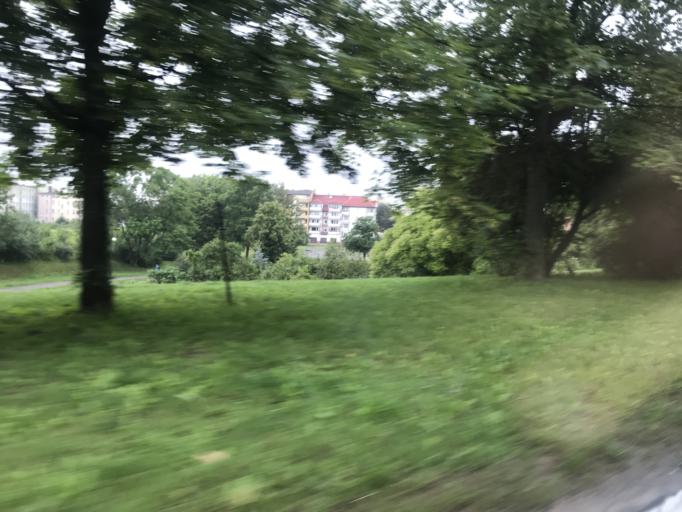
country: PL
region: Warmian-Masurian Voivodeship
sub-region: Powiat elblaski
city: Elblag
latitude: 54.1627
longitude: 19.4170
